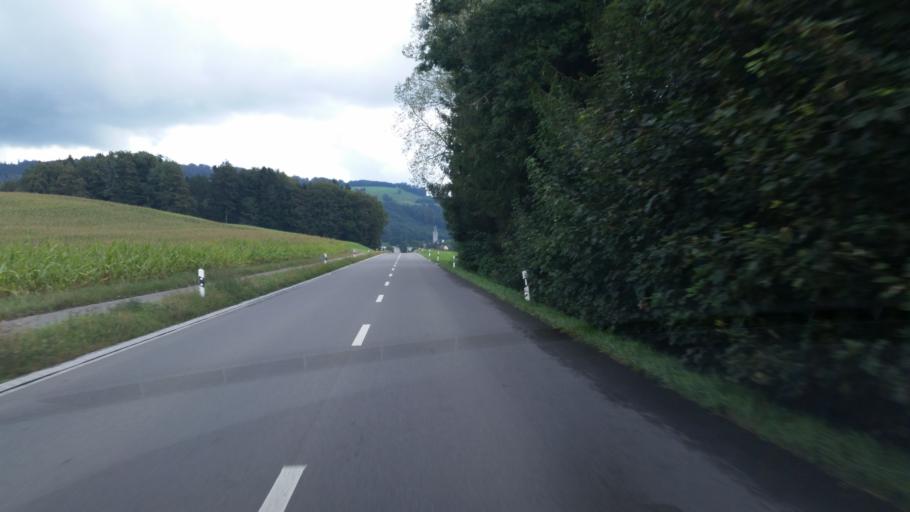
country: CH
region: Zurich
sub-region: Bezirk Affoltern
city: Hausen am Albis / Hausen (Dorf)
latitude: 47.2432
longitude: 8.5100
